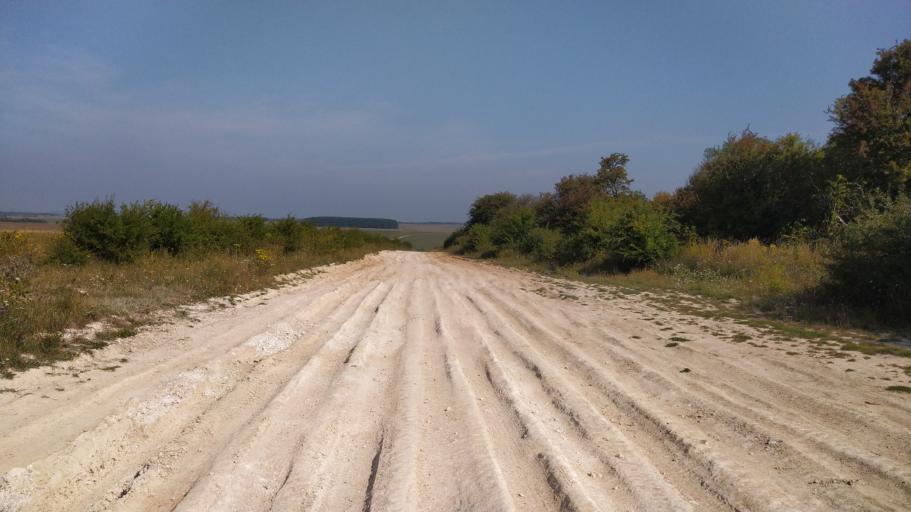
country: GB
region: England
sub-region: Wiltshire
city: Shrewton
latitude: 51.1862
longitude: -1.9525
